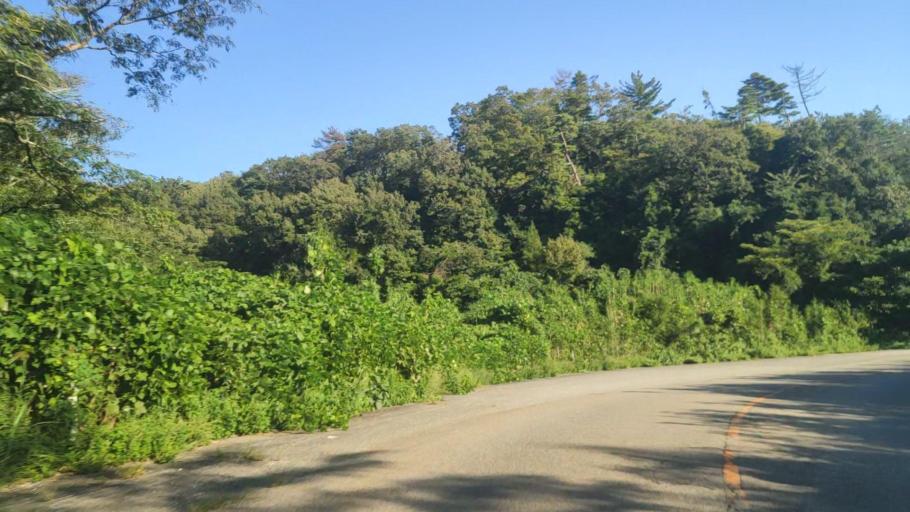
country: JP
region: Ishikawa
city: Nanao
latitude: 37.1004
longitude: 136.9498
